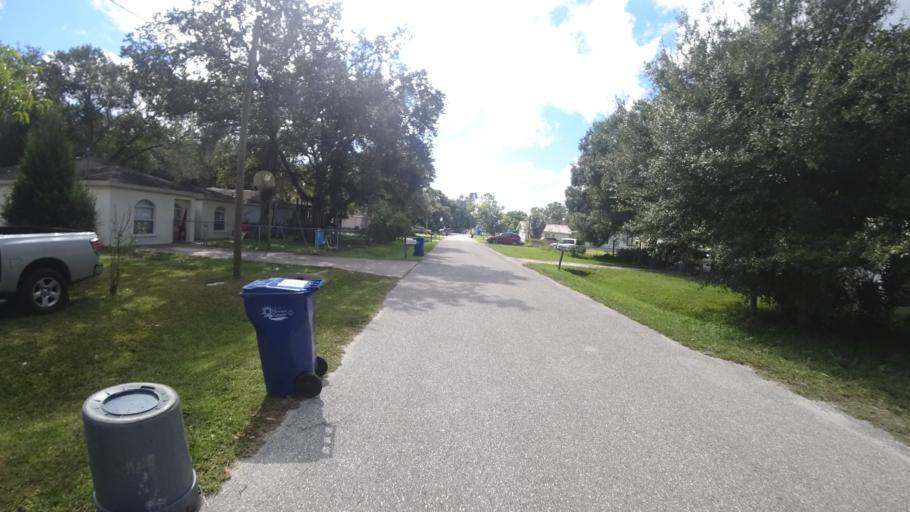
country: US
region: Florida
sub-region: Manatee County
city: West Samoset
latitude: 27.4745
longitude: -82.5569
